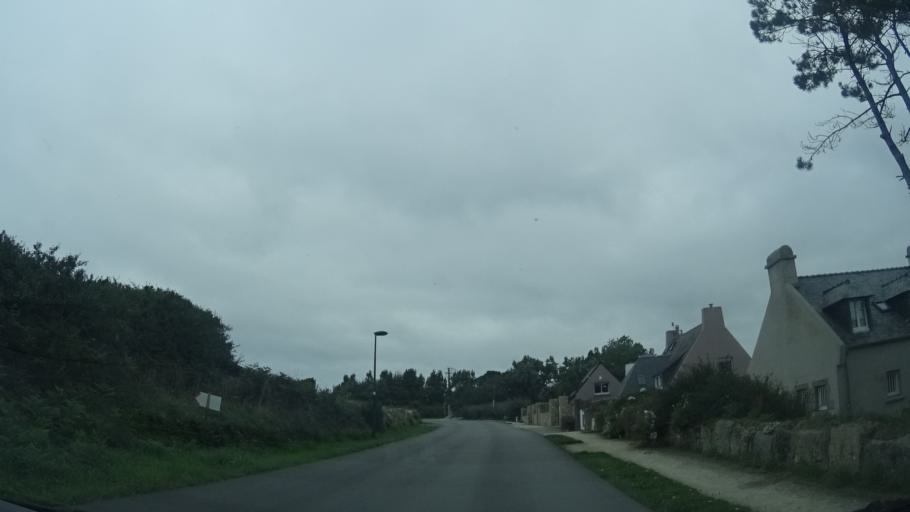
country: FR
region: Brittany
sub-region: Departement du Finistere
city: Lampaul-Plouarzel
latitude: 48.4724
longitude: -4.7569
